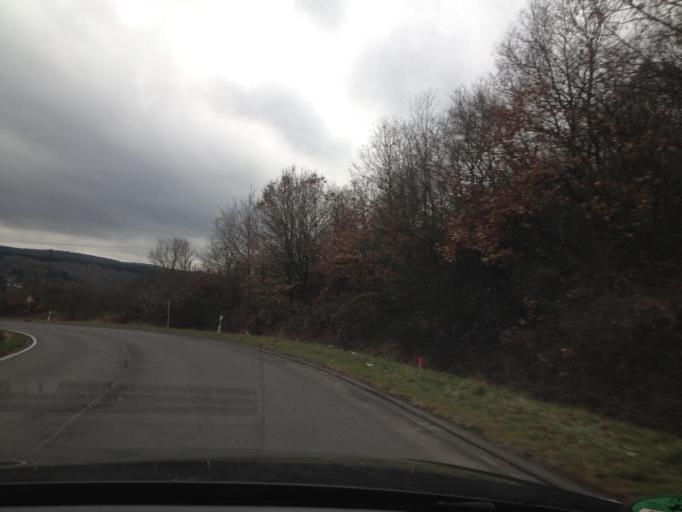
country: DE
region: Rheinland-Pfalz
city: Hintertiefenbach
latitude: 49.7169
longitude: 7.3653
